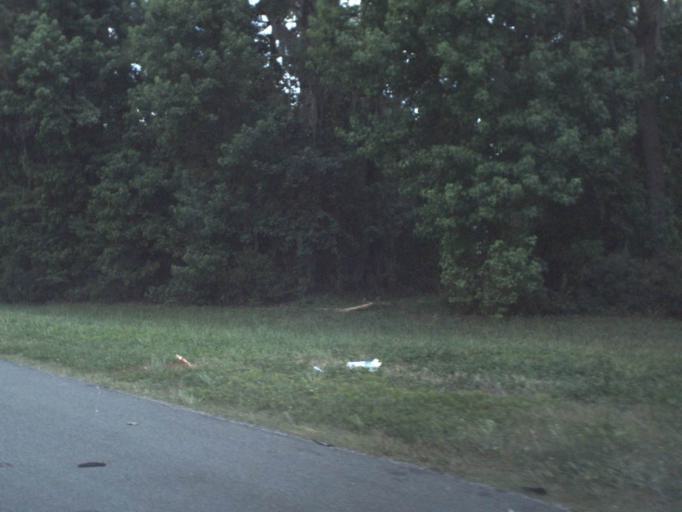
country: US
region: Florida
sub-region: Hamilton County
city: Jasper
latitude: 30.4083
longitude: -82.8915
